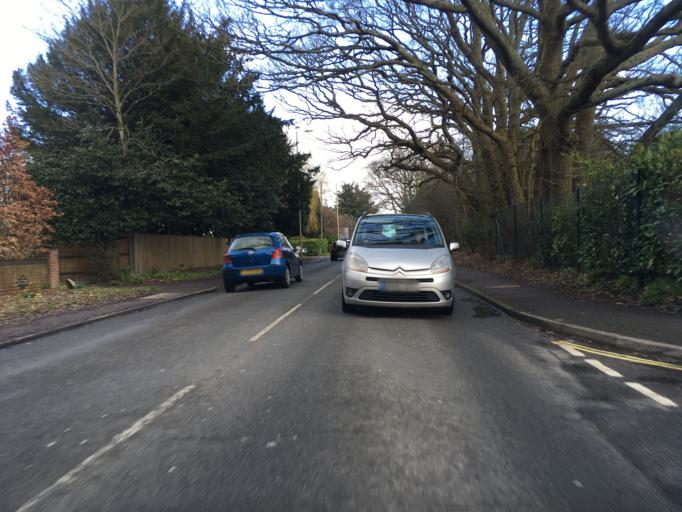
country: GB
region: England
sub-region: Hampshire
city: Eastleigh
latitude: 50.9731
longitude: -1.3890
